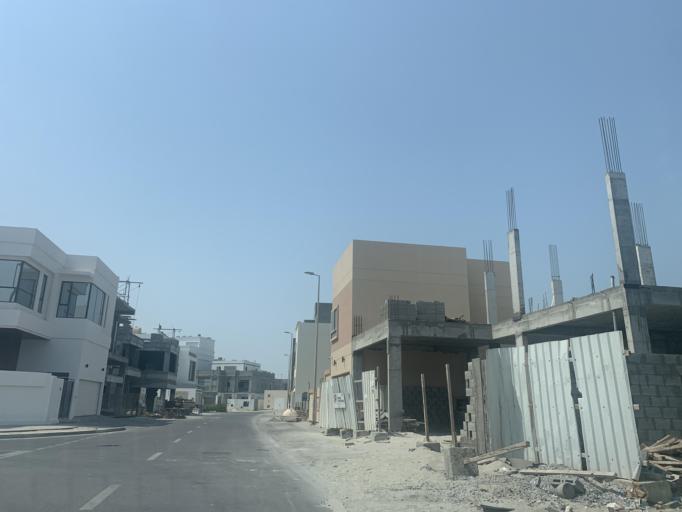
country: BH
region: Muharraq
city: Al Hadd
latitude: 26.2380
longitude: 50.6630
